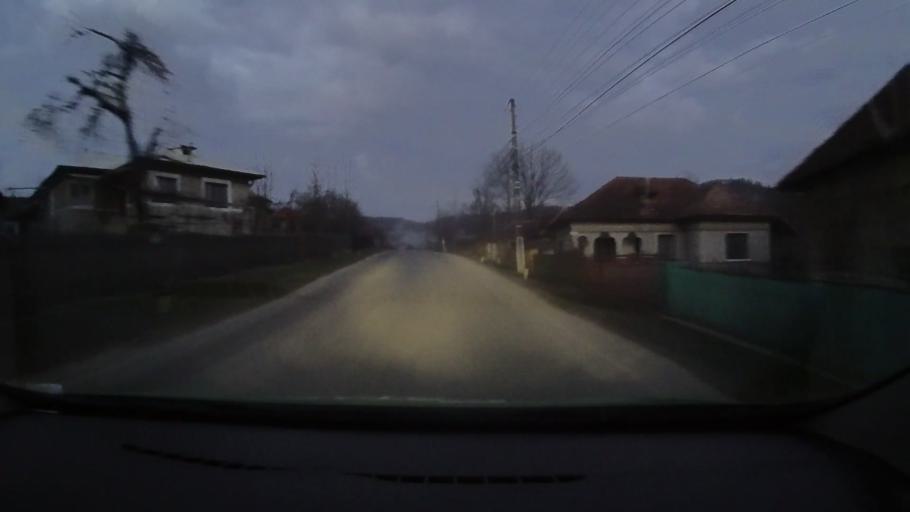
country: RO
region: Prahova
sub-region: Comuna Poiana Campina
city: Poiana Campina
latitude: 45.1204
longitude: 25.6698
